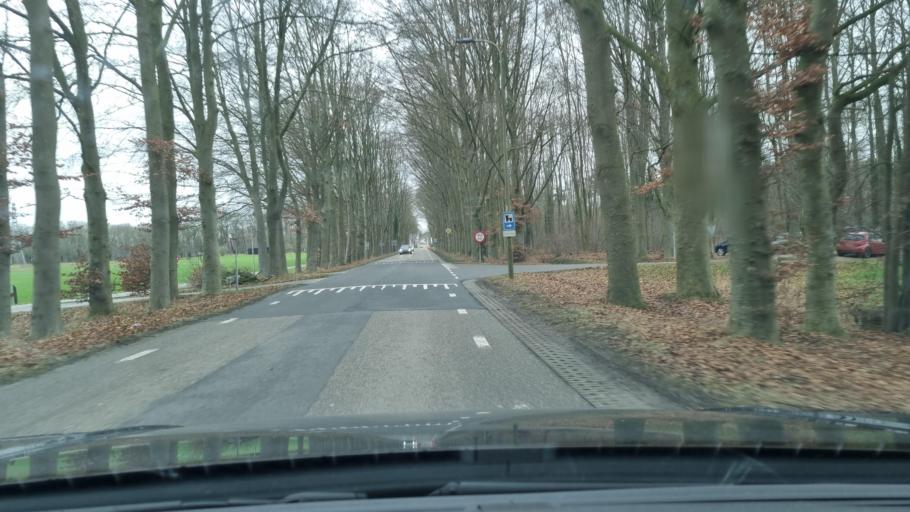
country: NL
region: Gelderland
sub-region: Gemeente Zutphen
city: Warnsveld
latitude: 52.1520
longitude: 6.2363
